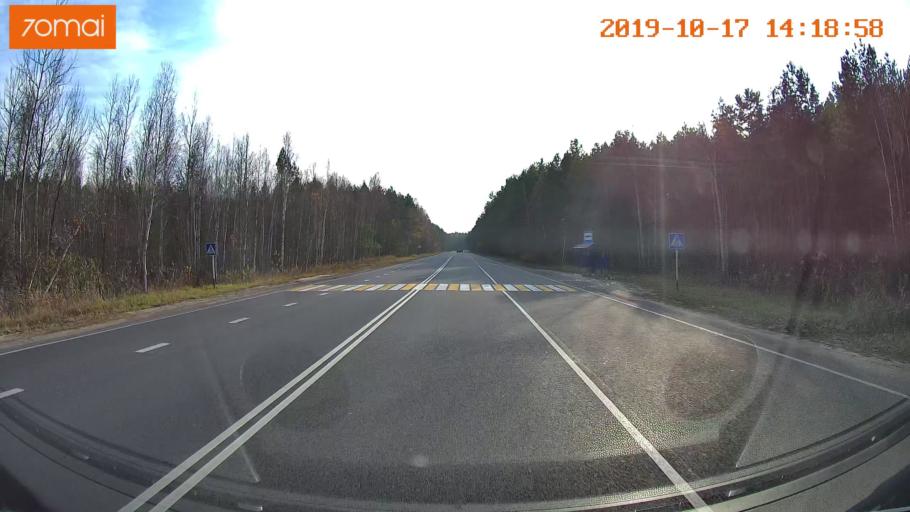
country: RU
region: Rjazan
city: Spas-Klepiki
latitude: 55.0563
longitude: 40.0249
